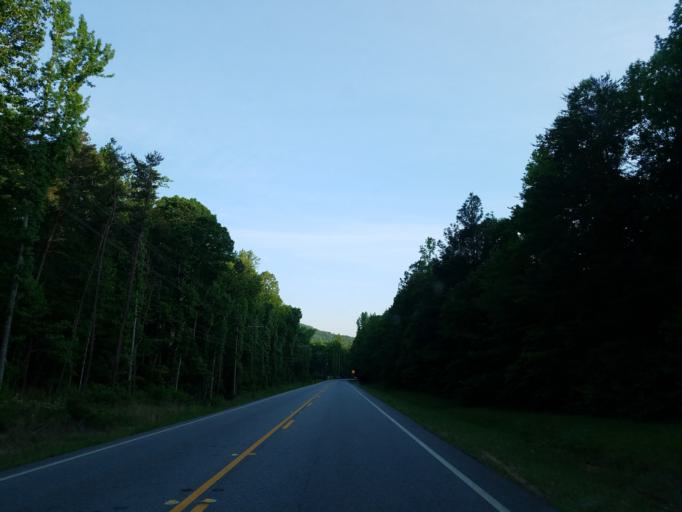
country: US
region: Georgia
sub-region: Whitfield County
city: Dalton
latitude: 34.6610
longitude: -85.0595
